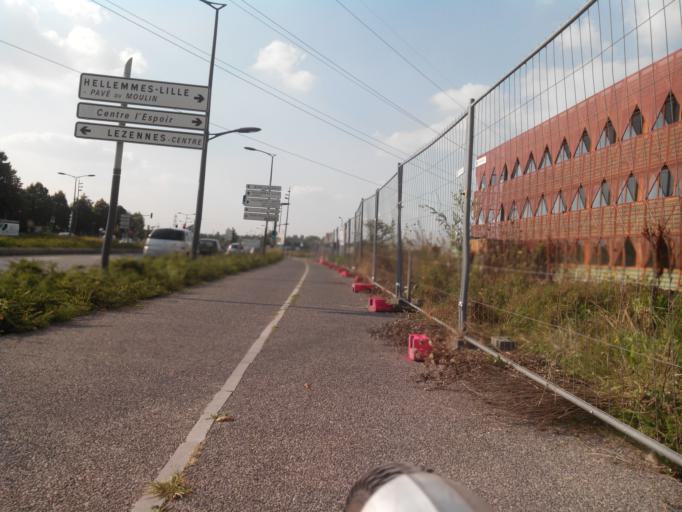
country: FR
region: Nord-Pas-de-Calais
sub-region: Departement du Nord
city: Lezennes
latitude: 50.6170
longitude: 3.1193
